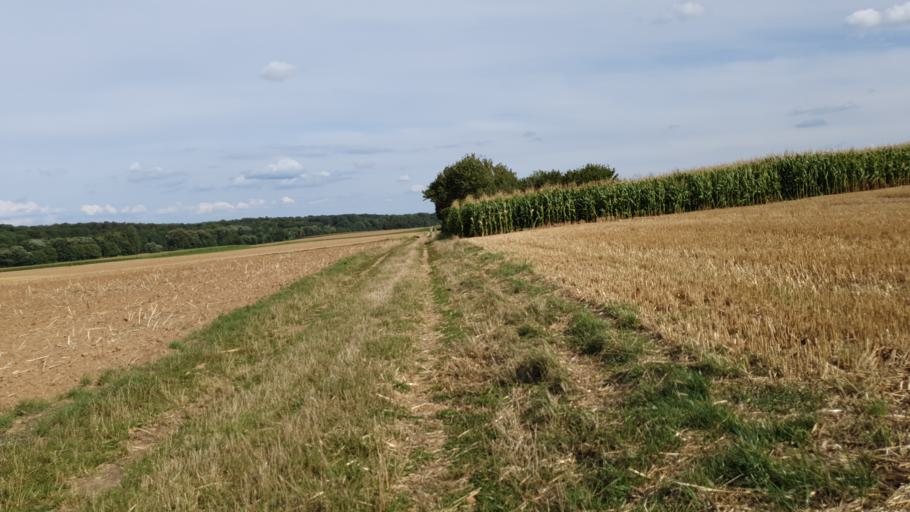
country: DE
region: Rheinland-Pfalz
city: Oberhausen
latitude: 49.1109
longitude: 8.0588
